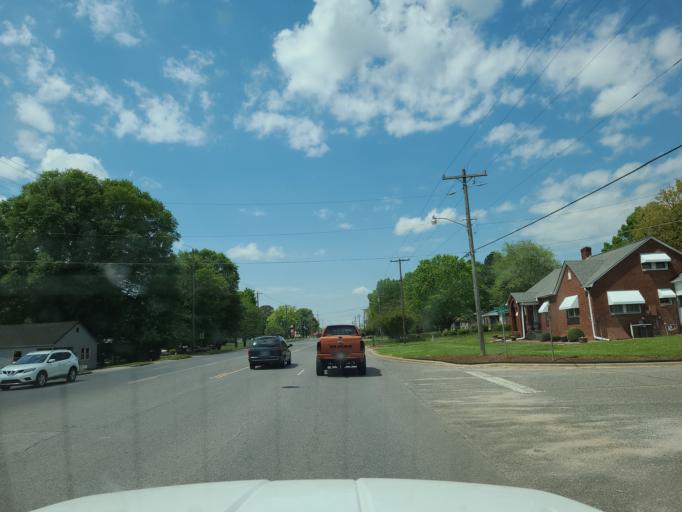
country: US
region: North Carolina
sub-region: Gaston County
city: Cherryville
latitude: 35.3872
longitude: -81.3580
